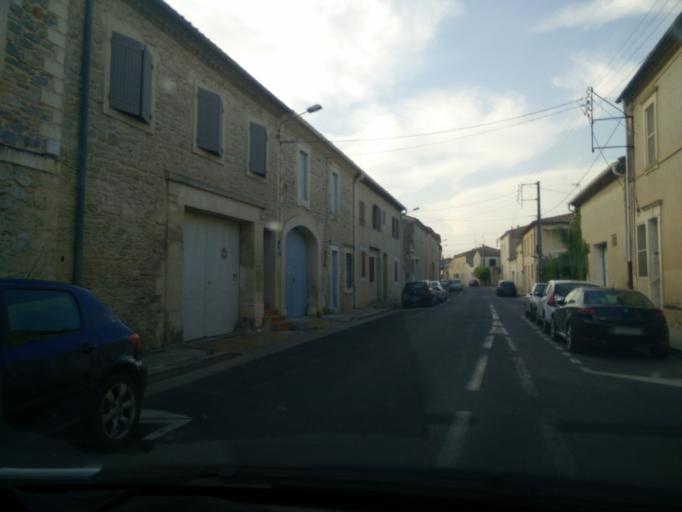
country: FR
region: Languedoc-Roussillon
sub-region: Departement de l'Herault
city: Marsillargues
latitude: 43.6677
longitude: 4.1778
